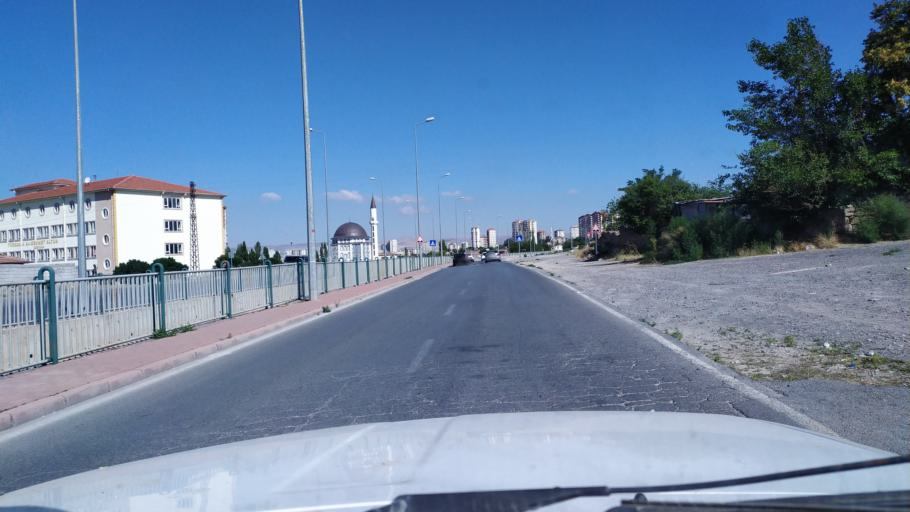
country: TR
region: Kayseri
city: Talas
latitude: 38.7289
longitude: 35.5501
